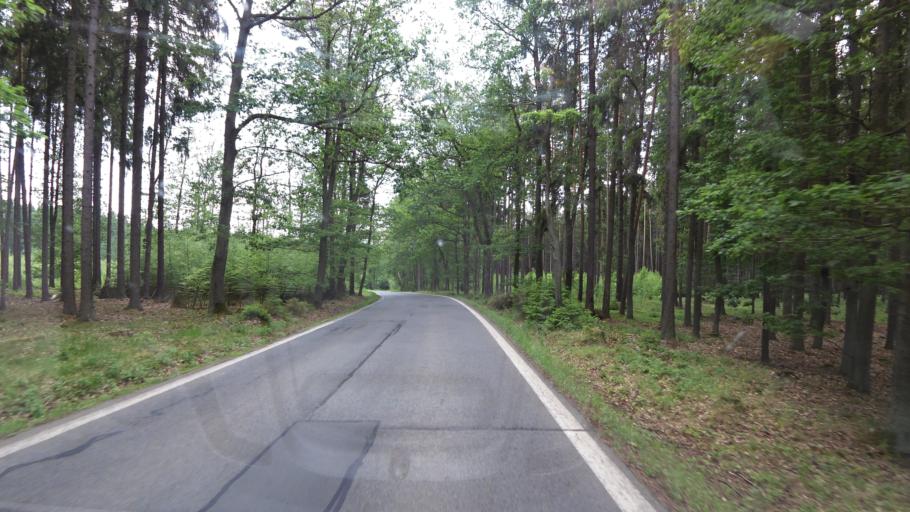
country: CZ
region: Plzensky
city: St'ahlavy
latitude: 49.6926
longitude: 13.5175
